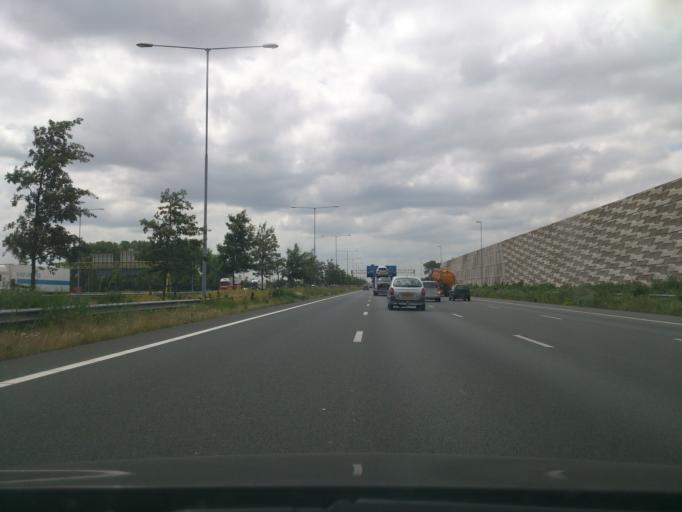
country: NL
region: North Brabant
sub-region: Gemeente 's-Hertogenbosch
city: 's-Hertogenbosch
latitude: 51.6917
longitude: 5.3498
